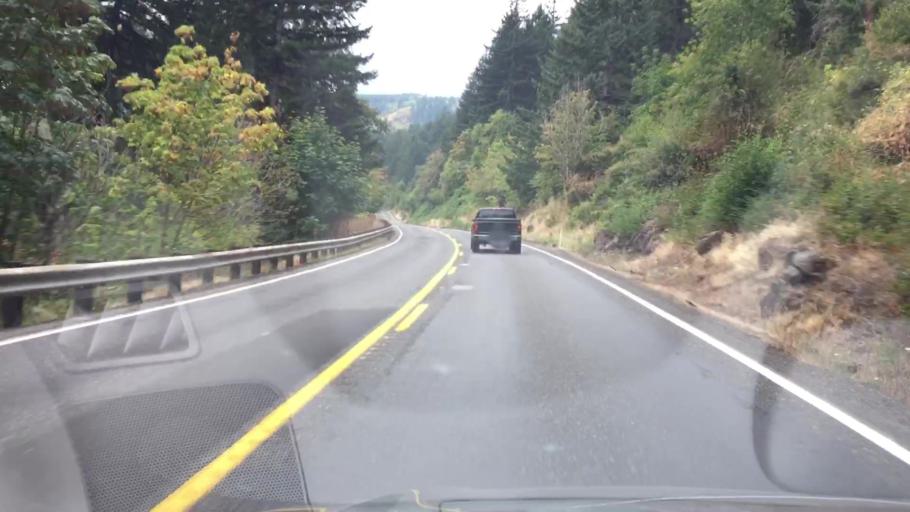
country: US
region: Washington
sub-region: Skamania County
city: Carson
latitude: 45.7167
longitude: -121.8067
